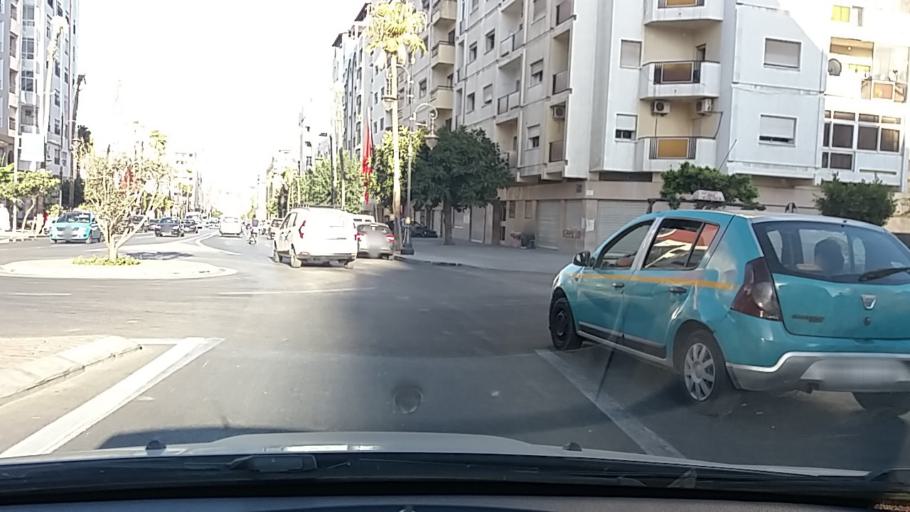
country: MA
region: Tanger-Tetouan
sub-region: Tanger-Assilah
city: Tangier
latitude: 35.7707
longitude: -5.8114
